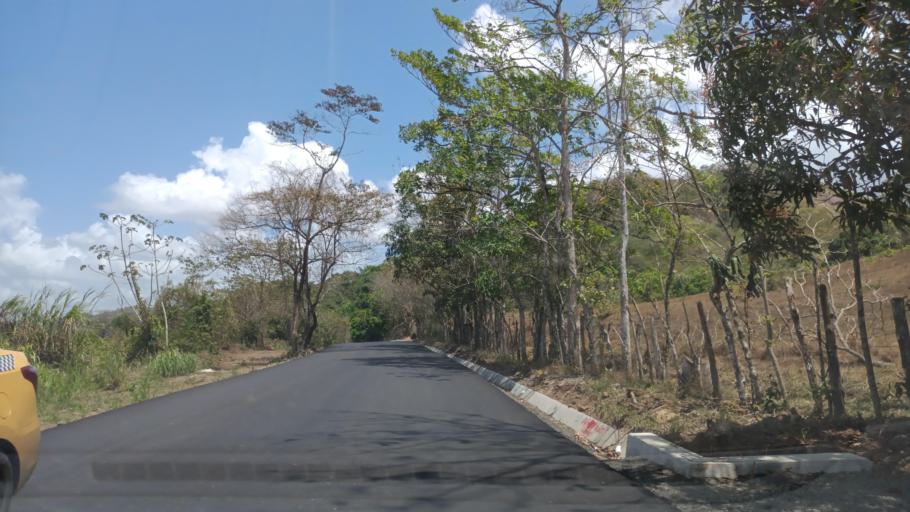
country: PA
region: Panama
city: Alcalde Diaz
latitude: 9.0885
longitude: -79.5776
